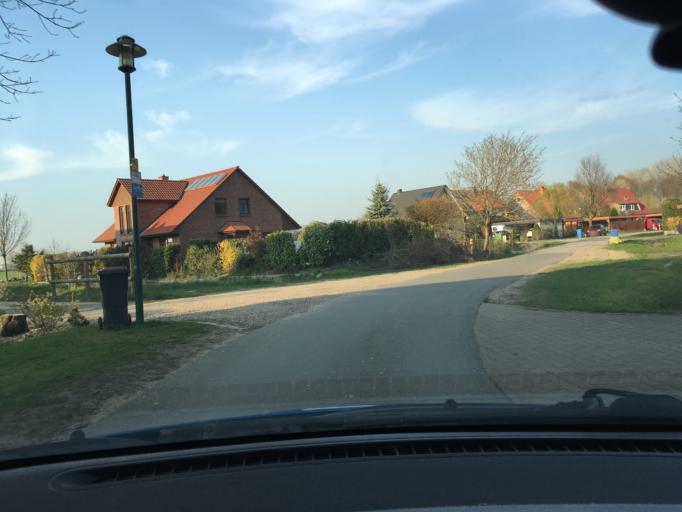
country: DE
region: Lower Saxony
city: Handorf
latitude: 53.3672
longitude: 10.3294
